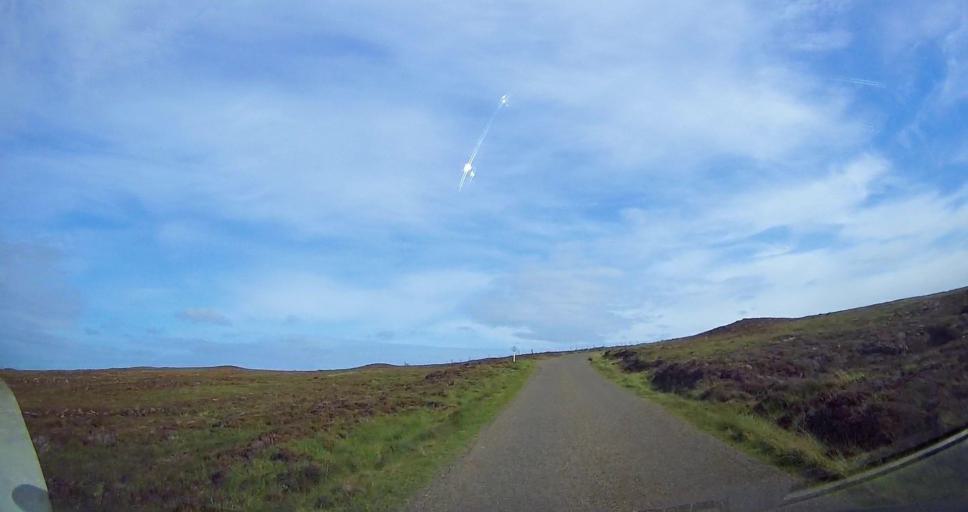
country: GB
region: Scotland
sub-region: Orkney Islands
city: Stromness
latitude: 58.8671
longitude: -3.2208
